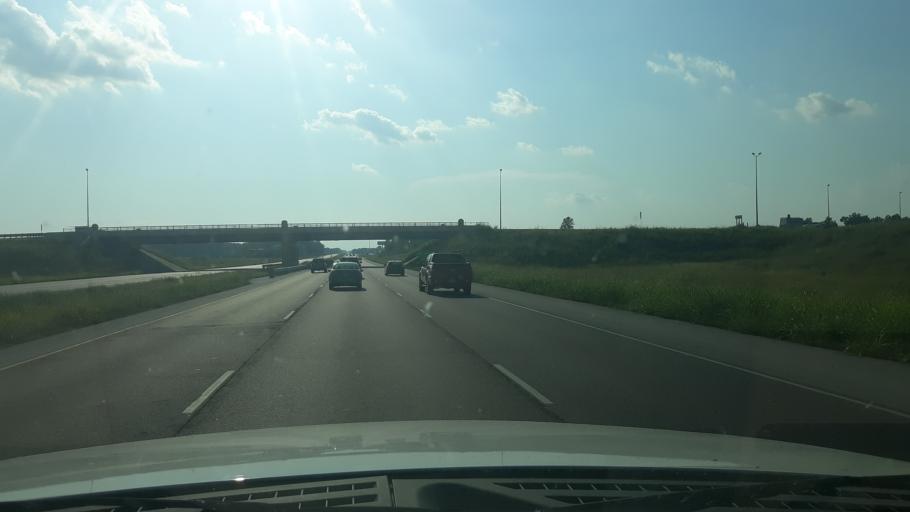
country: US
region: Illinois
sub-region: Williamson County
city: Crainville
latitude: 37.7452
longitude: -89.0563
